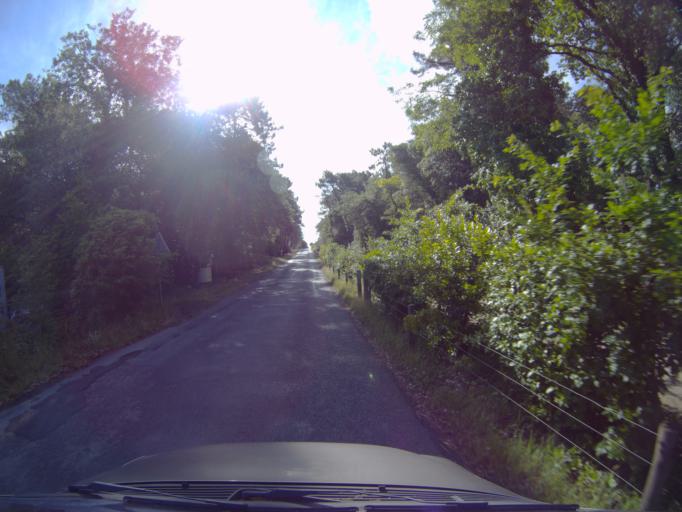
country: FR
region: Pays de la Loire
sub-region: Departement de la Vendee
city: La Barre-de-Monts
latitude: 46.8861
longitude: -2.1305
